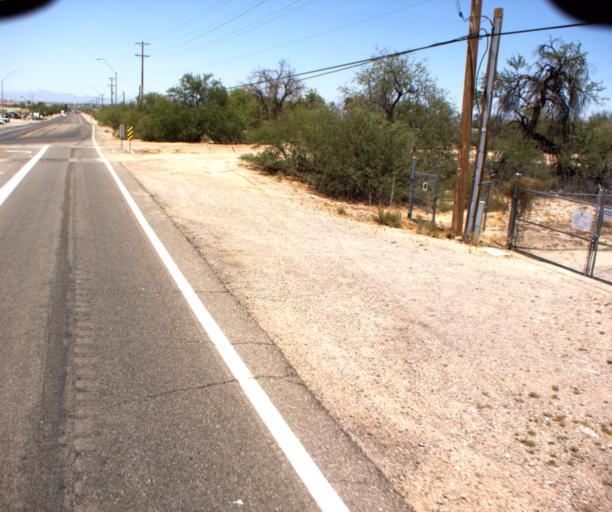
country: US
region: Arizona
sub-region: Pinal County
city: Florence
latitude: 33.0221
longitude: -111.3791
